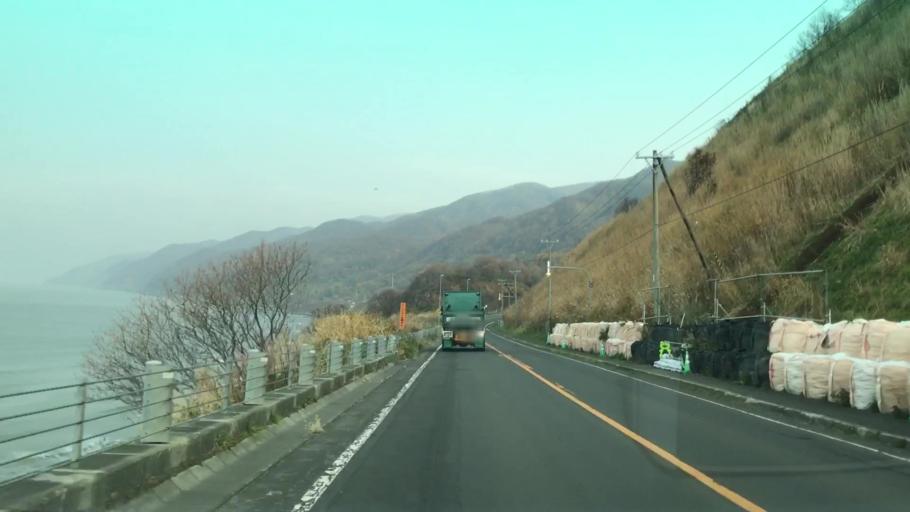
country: JP
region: Hokkaido
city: Ishikari
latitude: 43.4088
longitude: 141.4303
